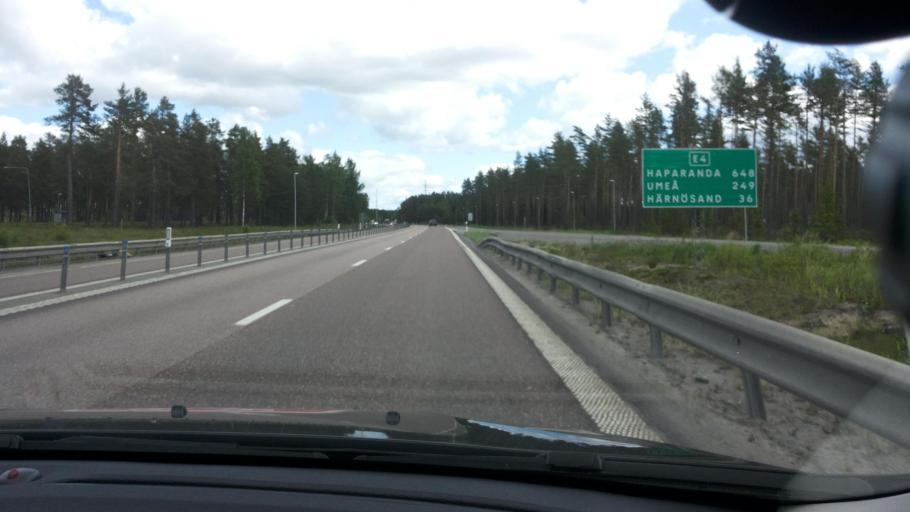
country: SE
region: Vaesternorrland
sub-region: Timra Kommun
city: Timra
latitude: 62.5043
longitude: 17.3526
